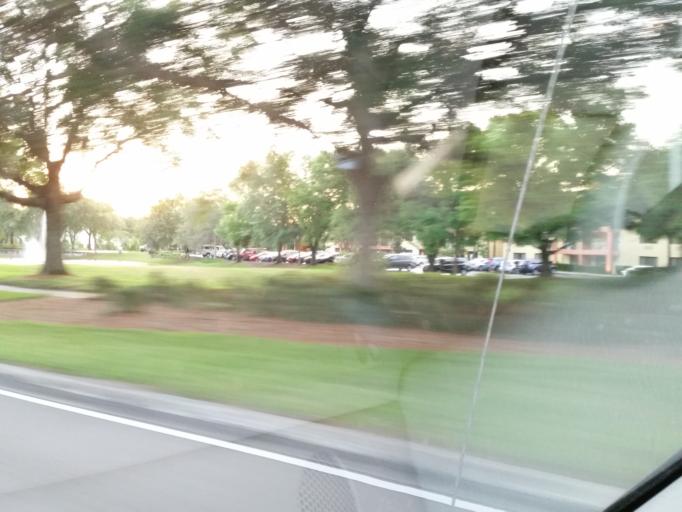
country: US
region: Florida
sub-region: Orange County
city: Doctor Phillips
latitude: 28.3860
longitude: -81.5008
